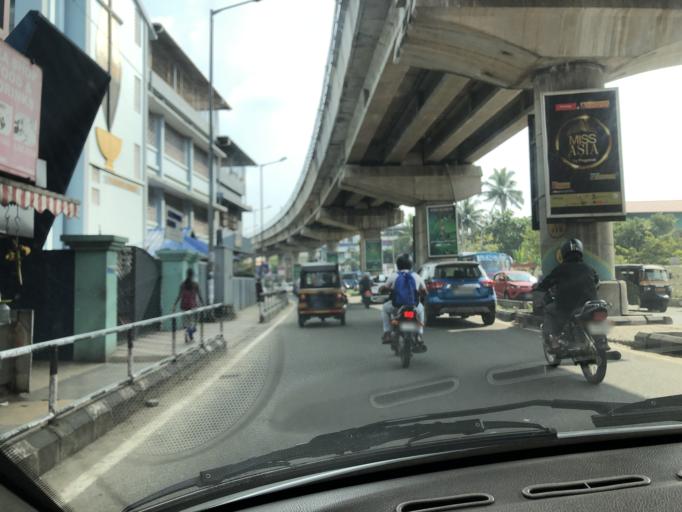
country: IN
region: Kerala
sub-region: Ernakulam
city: Cochin
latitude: 9.9864
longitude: 76.2835
